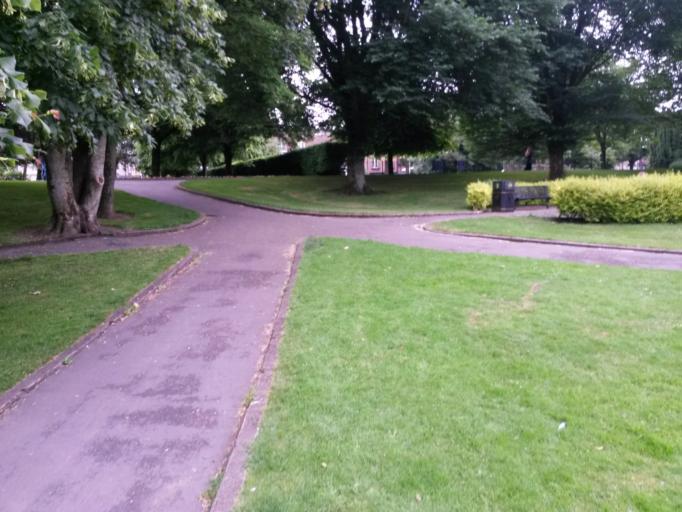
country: IE
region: Munster
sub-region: County Limerick
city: Luimneach
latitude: 52.6584
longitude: -8.6283
